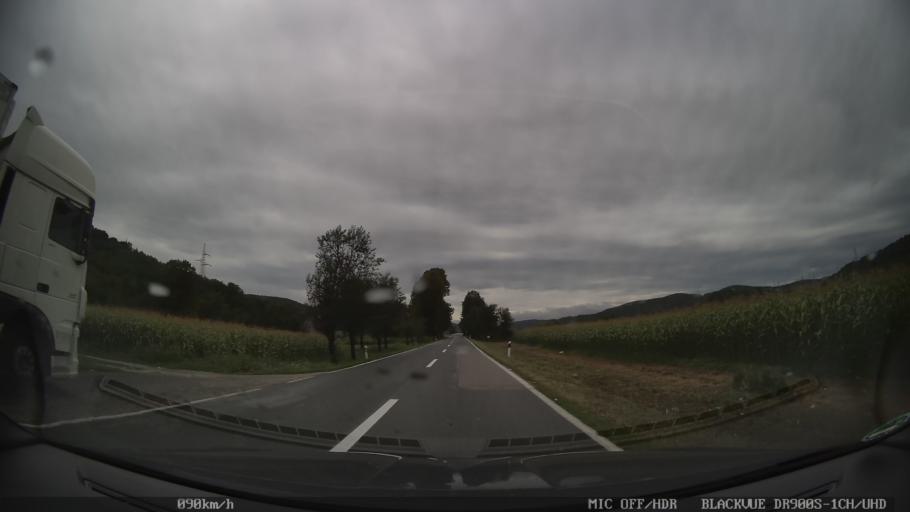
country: HR
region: Licko-Senjska
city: Brinje
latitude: 44.9219
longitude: 15.1435
